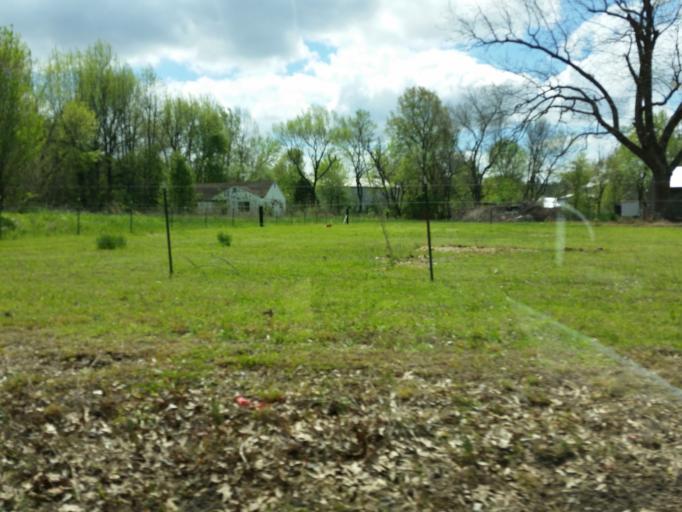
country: US
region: Arkansas
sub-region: Craighead County
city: Brookland
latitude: 36.0429
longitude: -90.6724
